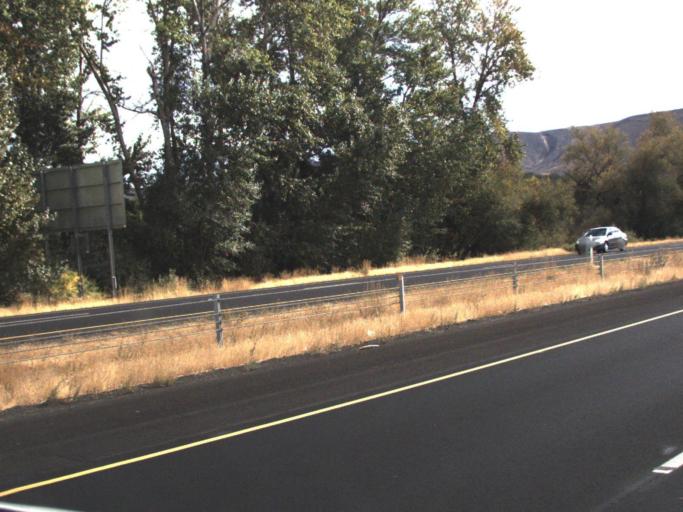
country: US
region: Washington
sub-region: Yakima County
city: Union Gap
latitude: 46.5519
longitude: -120.4706
